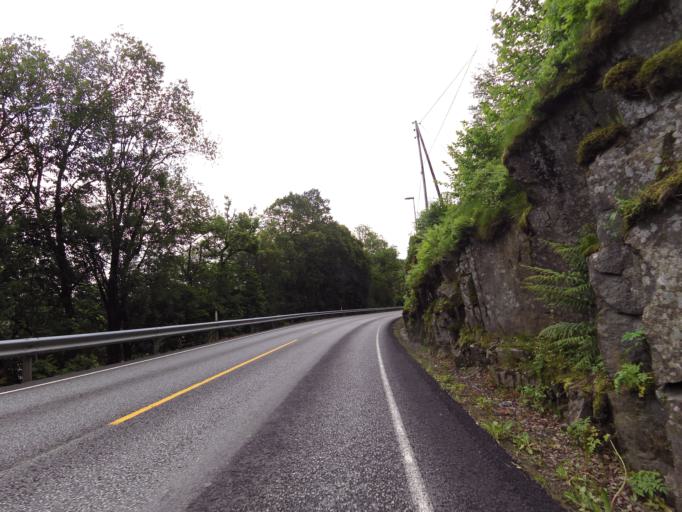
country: NO
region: Vest-Agder
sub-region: Lyngdal
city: Lyngdal
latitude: 58.1130
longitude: 6.9491
